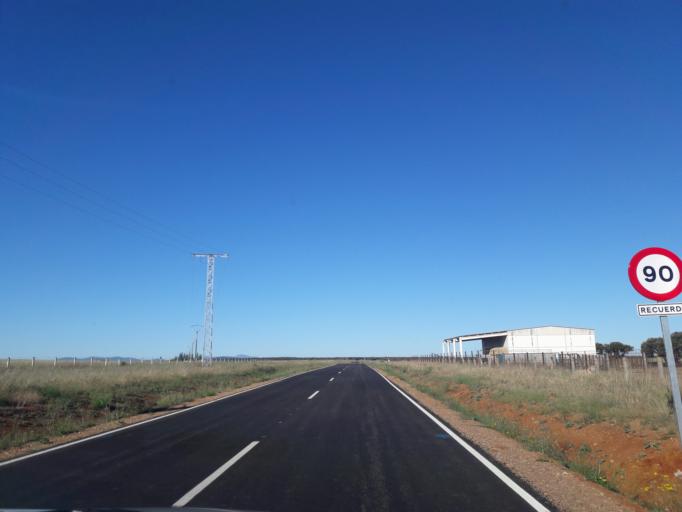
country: ES
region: Castille and Leon
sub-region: Provincia de Salamanca
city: Calzada de Don Diego
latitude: 40.8479
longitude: -5.8759
